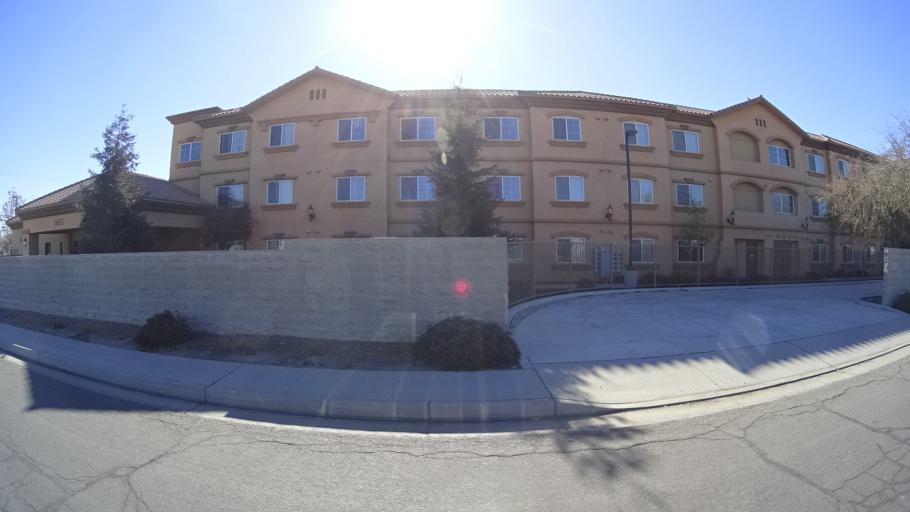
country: US
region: California
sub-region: Kern County
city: Bakersfield
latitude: 35.3684
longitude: -118.9770
